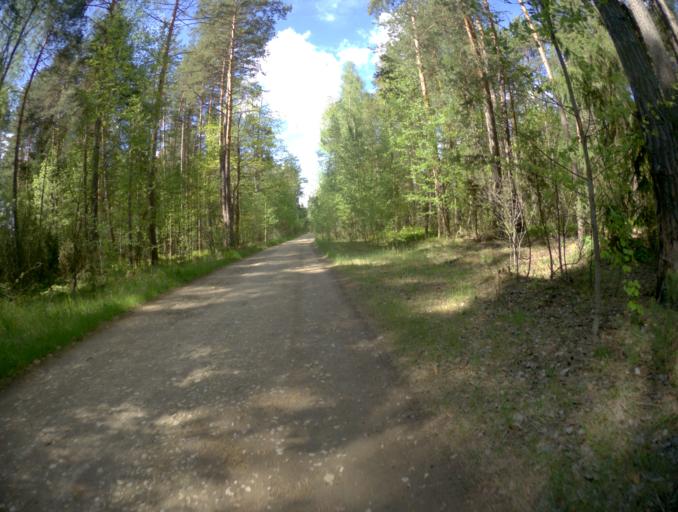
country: RU
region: Rjazan
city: Spas-Klepiki
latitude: 55.2453
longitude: 40.0744
